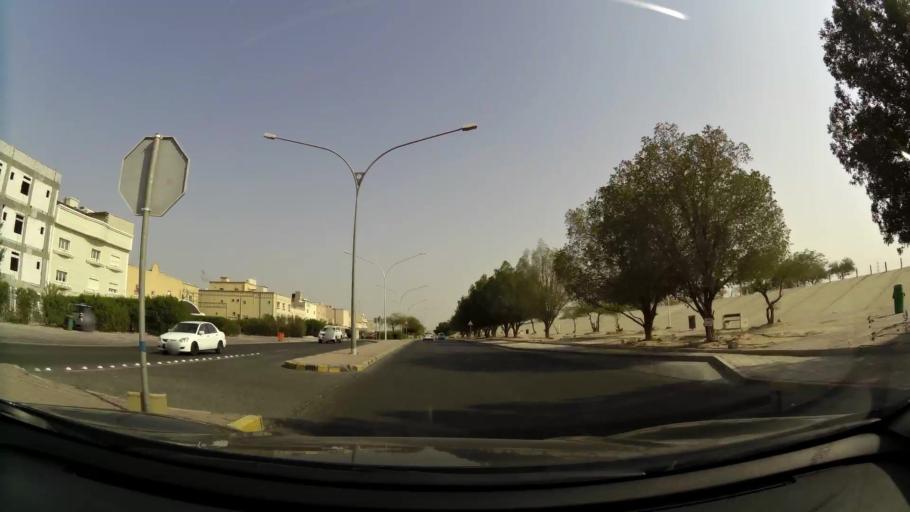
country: KW
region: Muhafazat al Jahra'
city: Al Jahra'
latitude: 29.3170
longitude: 47.6742
